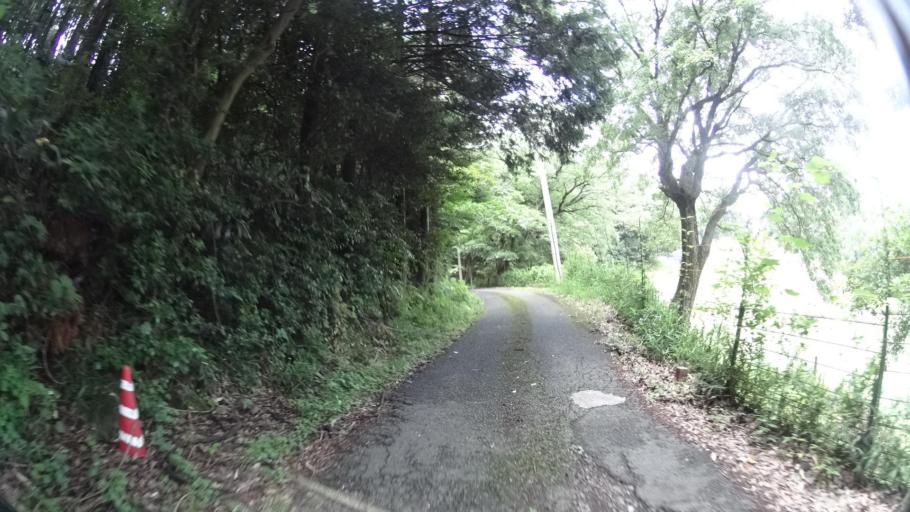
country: JP
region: Kyoto
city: Maizuru
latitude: 35.5312
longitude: 135.3412
